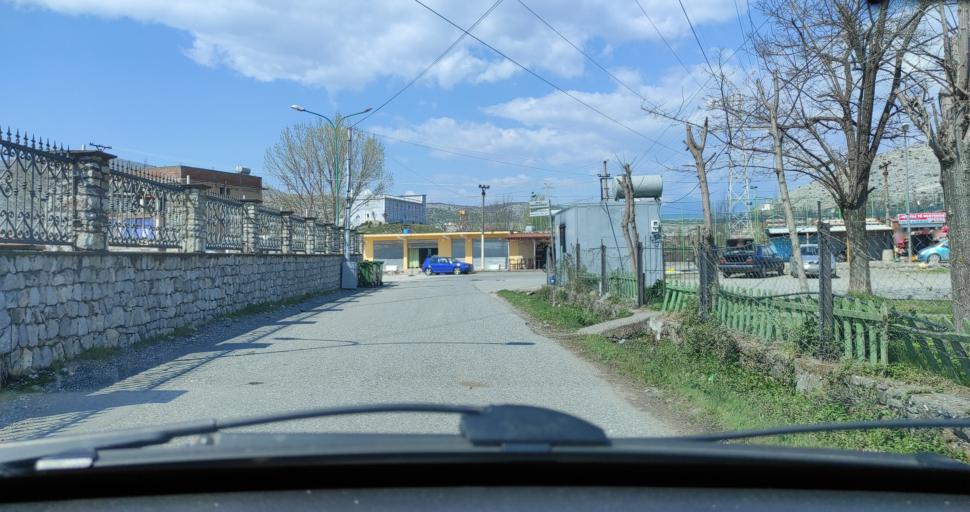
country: AL
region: Shkoder
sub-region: Rrethi i Shkodres
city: Vau i Dejes
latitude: 42.0073
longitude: 19.6413
